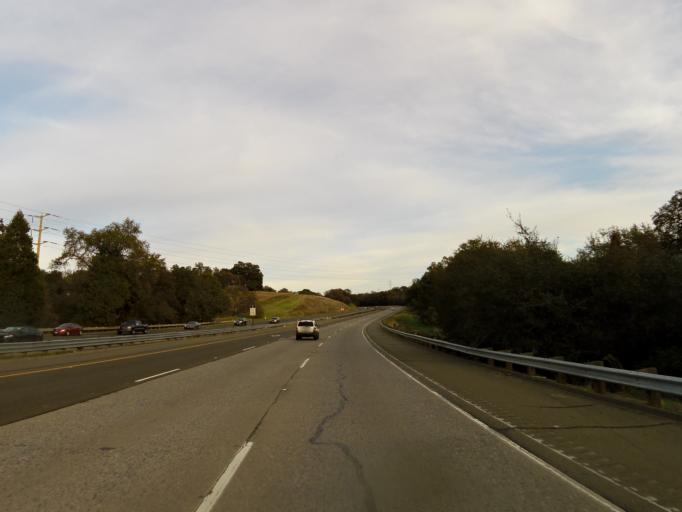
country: US
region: California
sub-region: El Dorado County
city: Cameron Park
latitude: 38.6574
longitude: -120.9925
